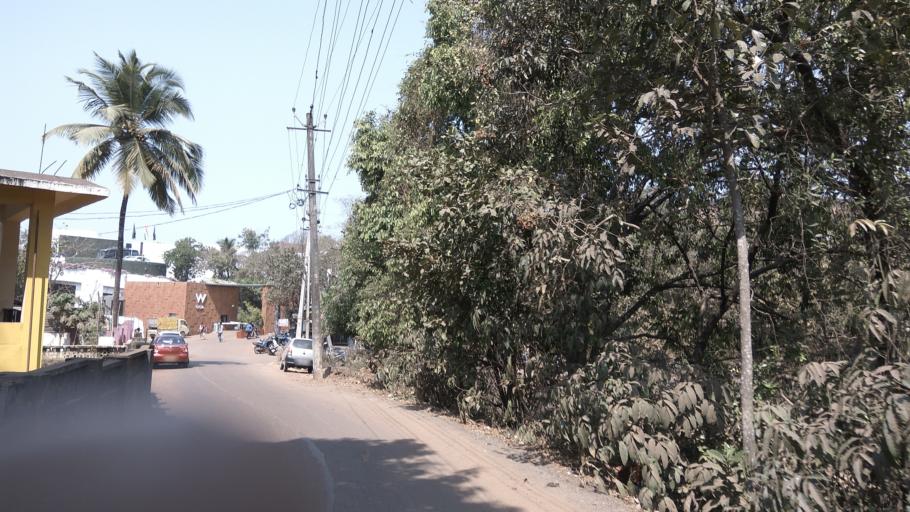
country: IN
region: Goa
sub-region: North Goa
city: Vagator
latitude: 15.6020
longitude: 73.7376
